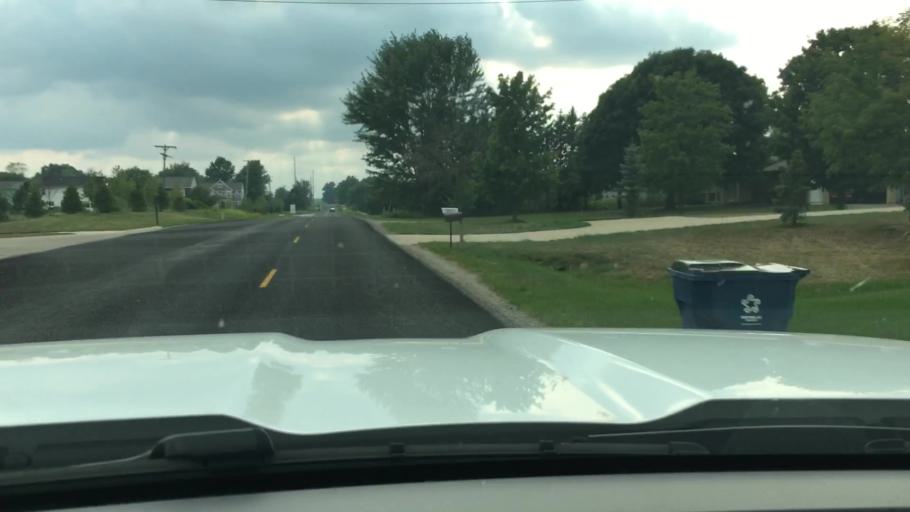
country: US
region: Michigan
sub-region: Ottawa County
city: Hudsonville
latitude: 42.8330
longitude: -85.8545
